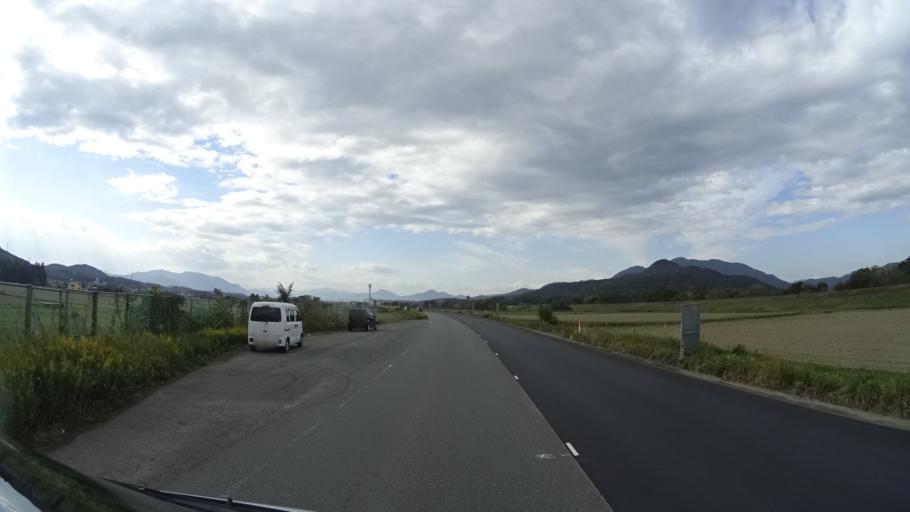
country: JP
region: Kyoto
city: Ayabe
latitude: 35.3075
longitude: 135.1906
